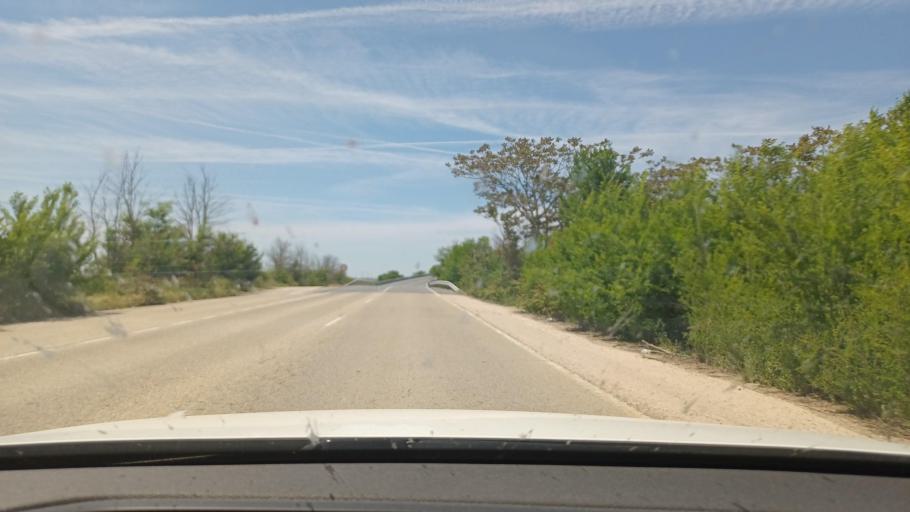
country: ES
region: Castille-La Mancha
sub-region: Provincia de Cuenca
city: Montalbo
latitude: 39.8842
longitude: -2.6798
